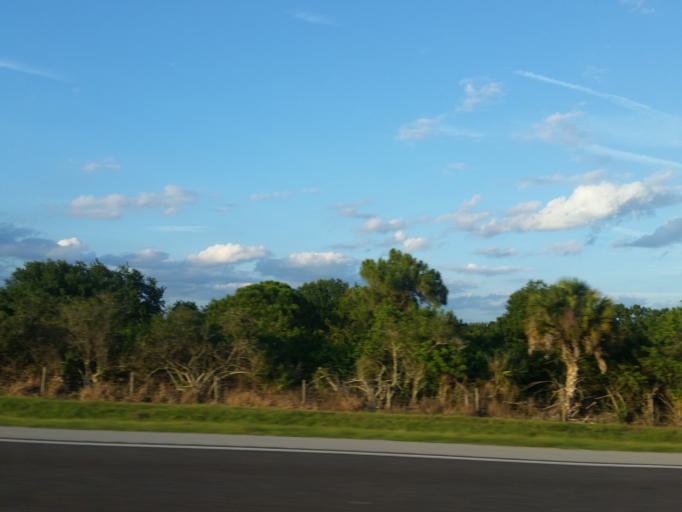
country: US
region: Florida
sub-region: Sarasota County
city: Laurel
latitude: 27.1584
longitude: -82.4254
